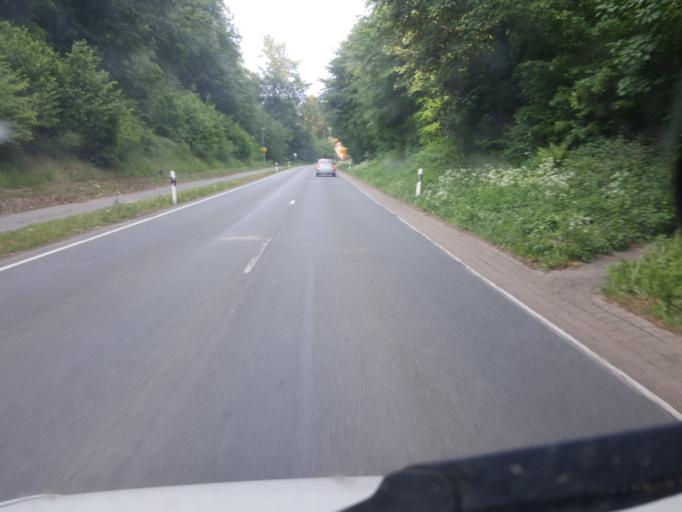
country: DE
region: Lower Saxony
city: Binnen
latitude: 52.6401
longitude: 9.1373
